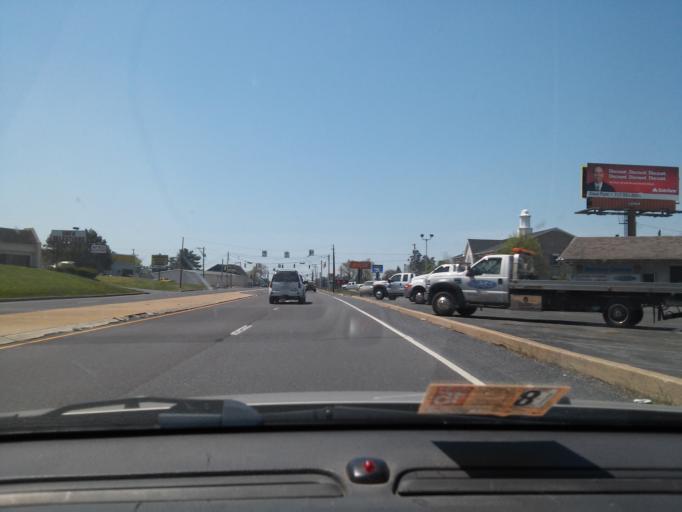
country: US
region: Pennsylvania
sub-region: Dauphin County
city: Paxtonia
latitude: 40.3188
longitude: -76.7945
